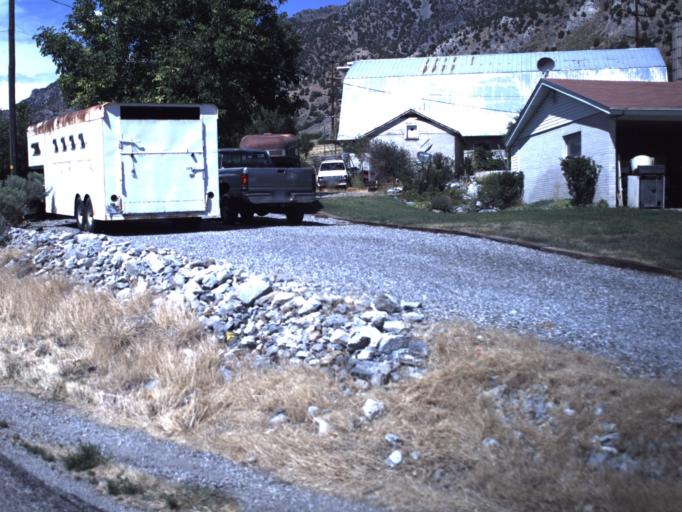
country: US
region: Utah
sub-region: Box Elder County
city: Brigham City
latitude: 41.5707
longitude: -112.0291
